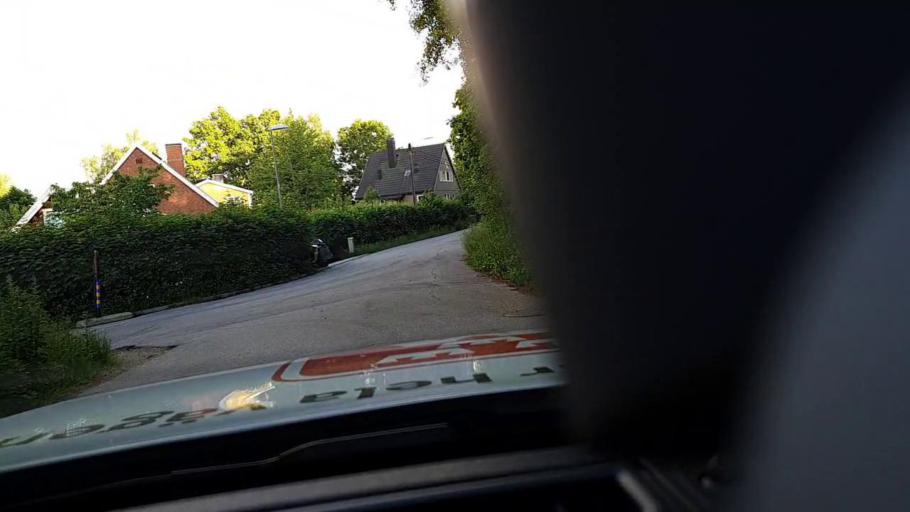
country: SE
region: Stockholm
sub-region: Huddinge Kommun
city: Huddinge
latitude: 59.2444
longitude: 17.9749
